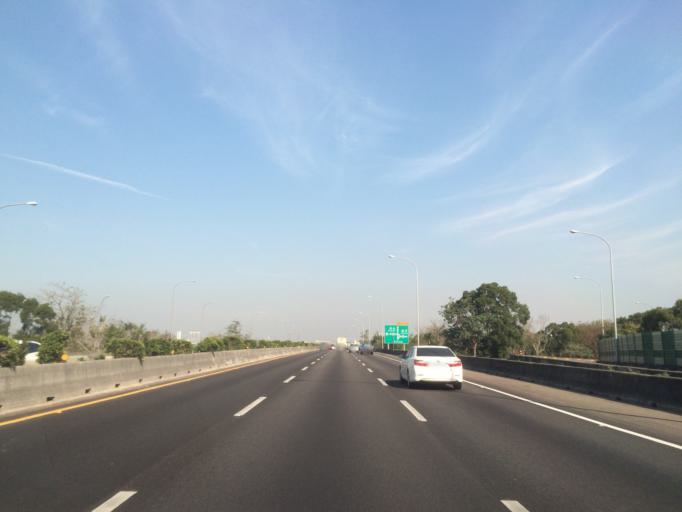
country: TW
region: Taiwan
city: Fengyuan
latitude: 24.2491
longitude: 120.6903
